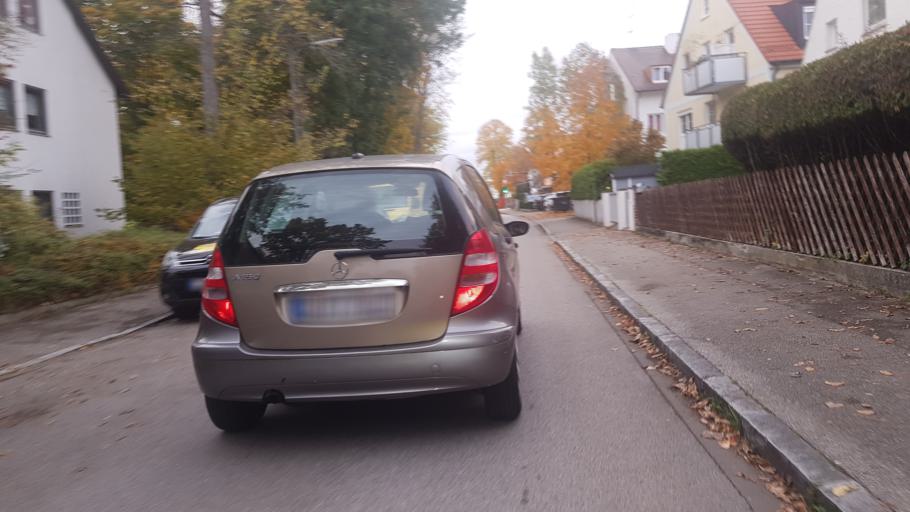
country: DE
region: Bavaria
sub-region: Upper Bavaria
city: Unterhaching
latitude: 48.0886
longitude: 11.6116
